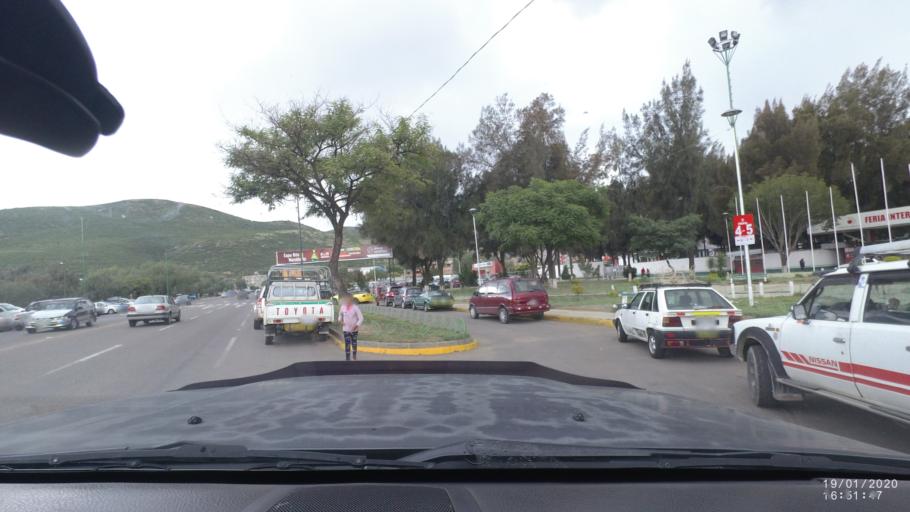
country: BO
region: Cochabamba
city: Cochabamba
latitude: -17.4177
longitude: -66.1298
